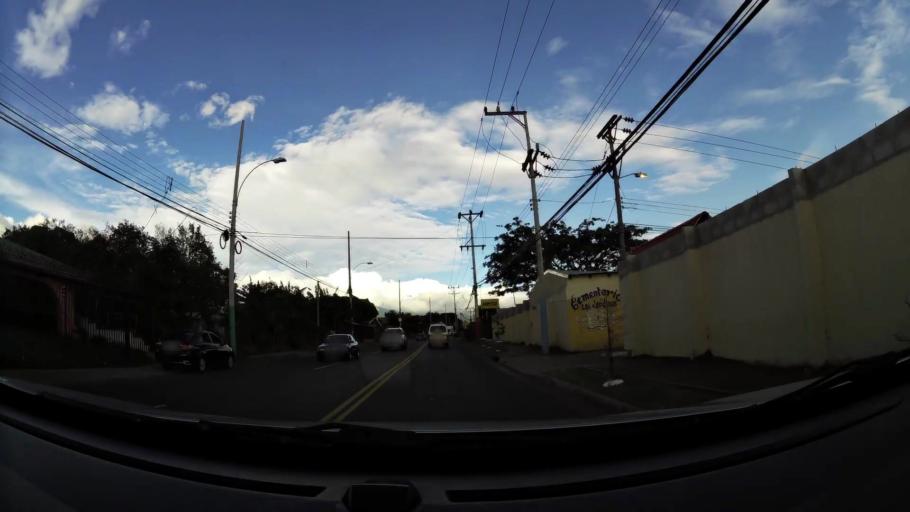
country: CR
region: Heredia
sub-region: Canton de Belen
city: San Antonio
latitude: 10.0013
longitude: -84.1920
